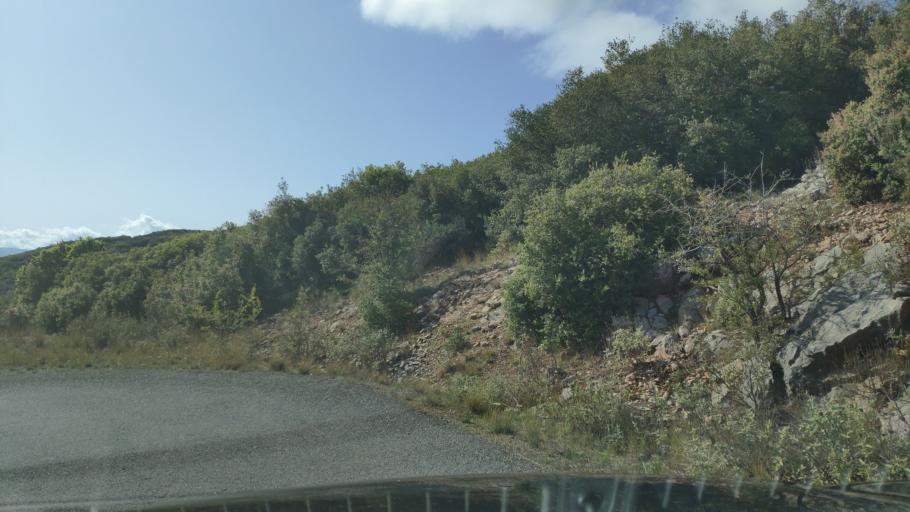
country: GR
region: Peloponnese
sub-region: Nomos Arkadias
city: Dimitsana
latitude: 37.5741
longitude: 22.0009
